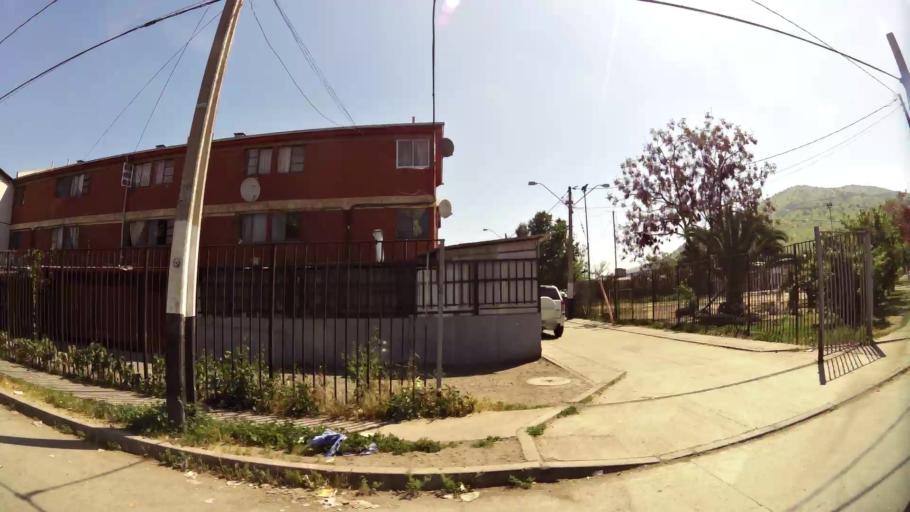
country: CL
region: Santiago Metropolitan
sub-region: Provincia de Santiago
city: Lo Prado
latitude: -33.4036
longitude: -70.7326
